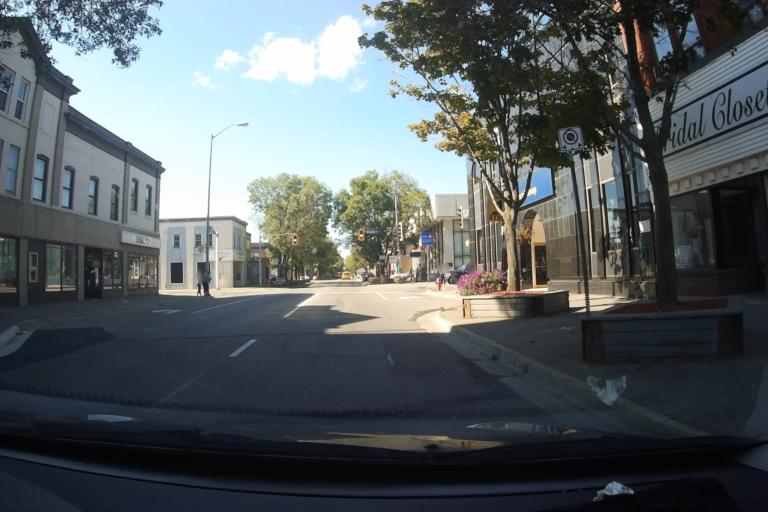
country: CA
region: Ontario
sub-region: Algoma
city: Sault Ste. Marie
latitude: 46.5089
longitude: -84.3295
